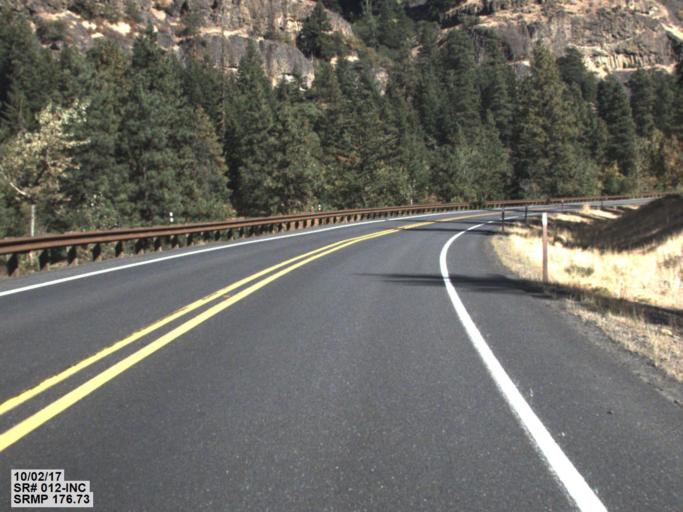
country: US
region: Washington
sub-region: Yakima County
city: Tieton
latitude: 46.6943
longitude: -120.9214
